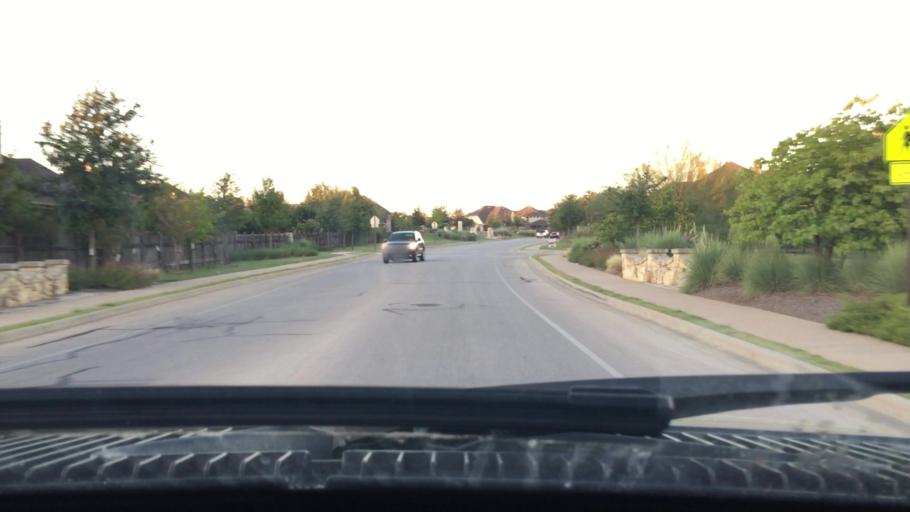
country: US
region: Texas
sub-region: Williamson County
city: Leander
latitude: 30.5368
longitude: -97.8646
